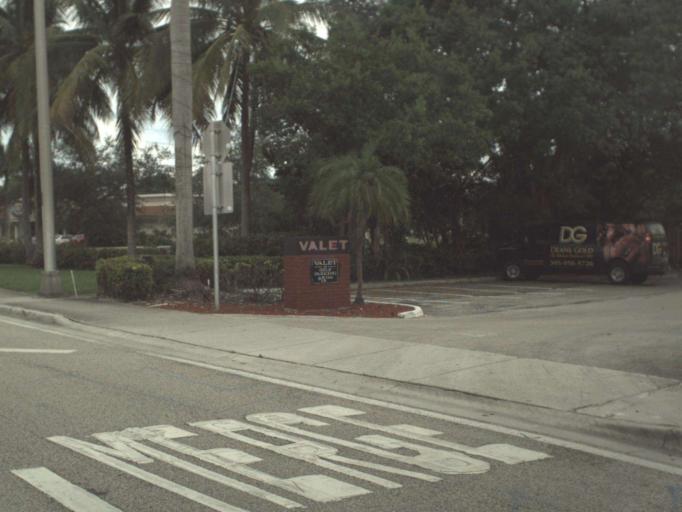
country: US
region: Florida
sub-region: Miami-Dade County
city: North Miami Beach
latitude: 25.9267
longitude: -80.1535
